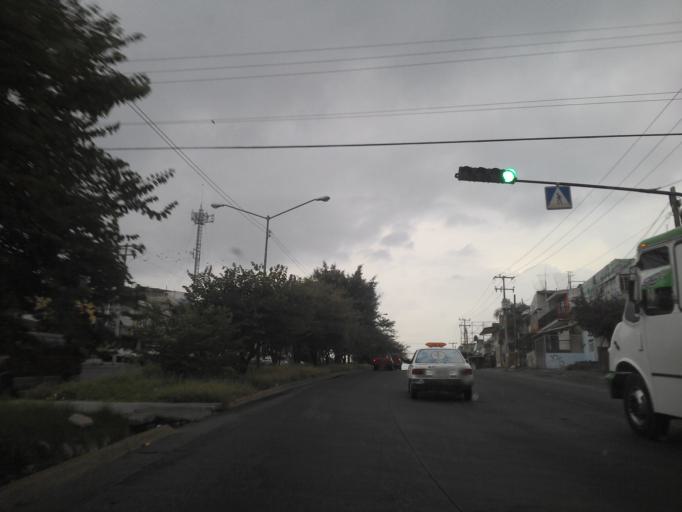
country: MX
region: Jalisco
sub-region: Tlajomulco de Zuniga
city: Altus Bosques
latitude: 20.6153
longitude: -103.3747
